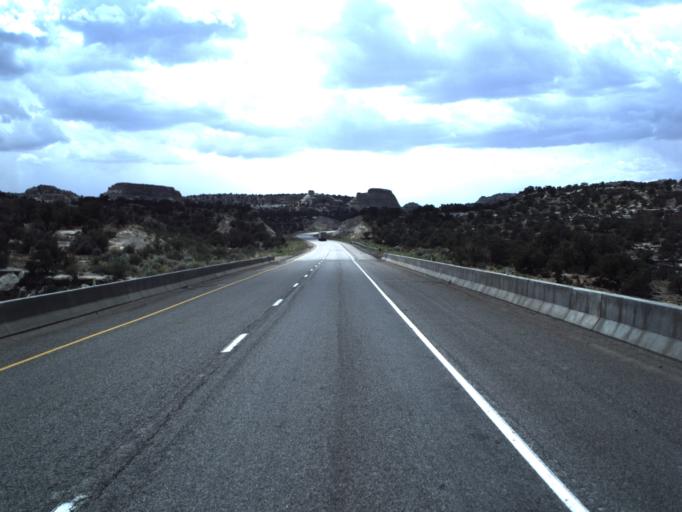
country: US
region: Utah
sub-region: Emery County
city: Ferron
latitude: 38.8609
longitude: -110.8660
